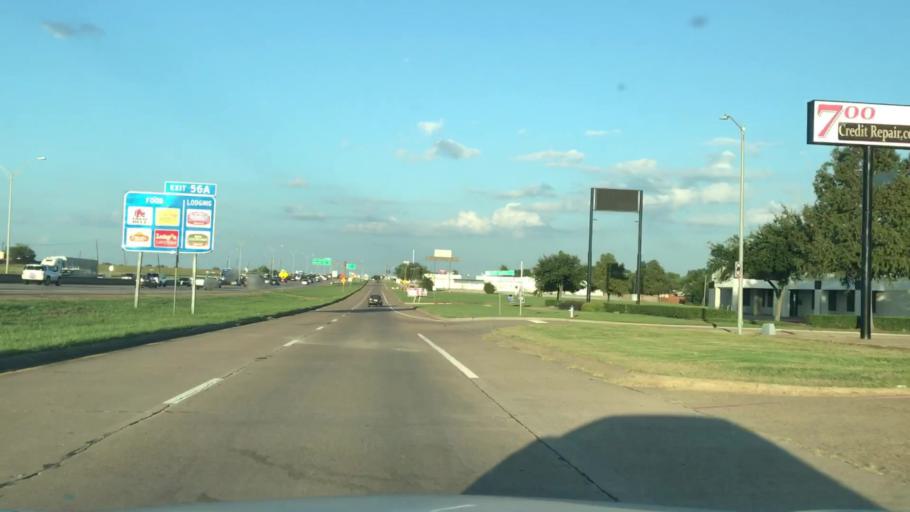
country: US
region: Texas
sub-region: Dallas County
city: Mesquite
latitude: 32.8130
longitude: -96.6476
